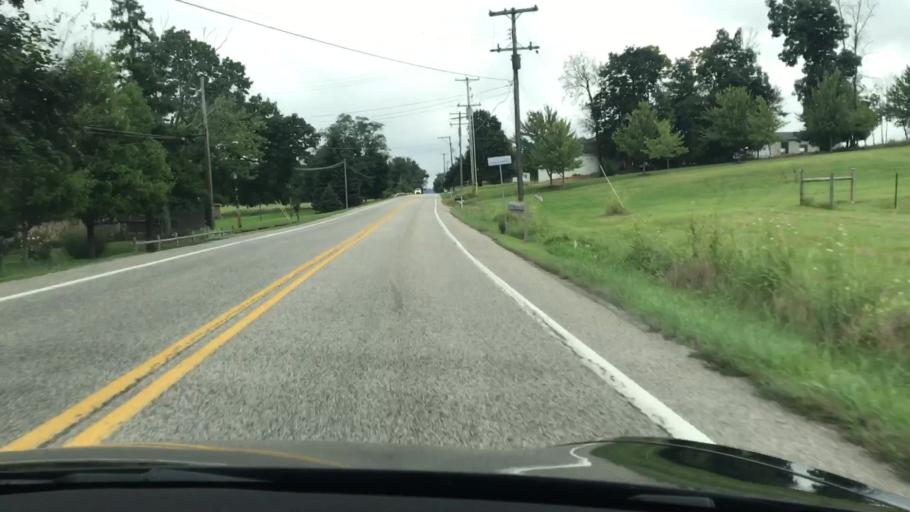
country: US
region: Pennsylvania
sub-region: Cumberland County
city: Shiremanstown
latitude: 40.1535
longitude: -76.9669
